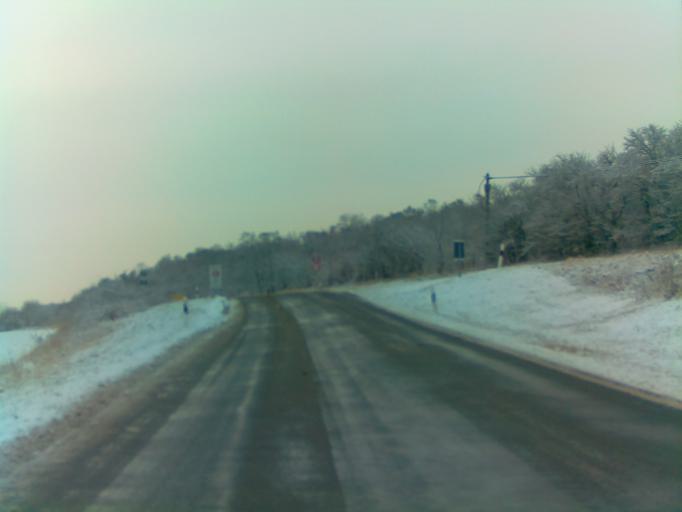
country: DE
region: Thuringia
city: Arnstadt
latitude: 50.8403
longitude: 10.9192
